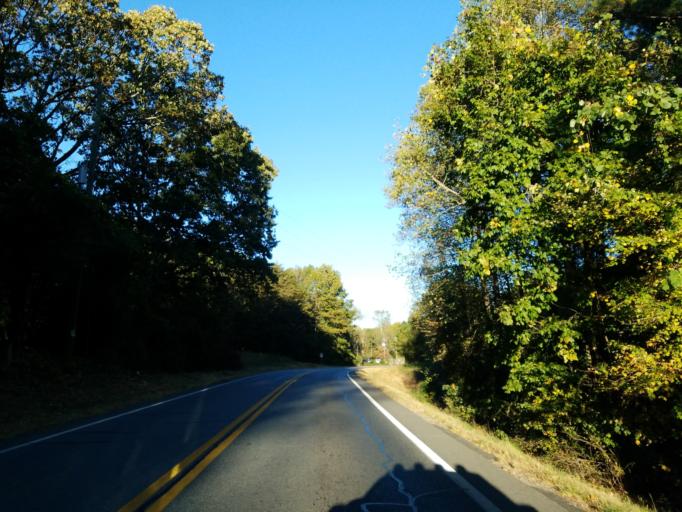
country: US
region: Georgia
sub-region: Dawson County
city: Dawsonville
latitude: 34.4204
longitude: -84.1362
